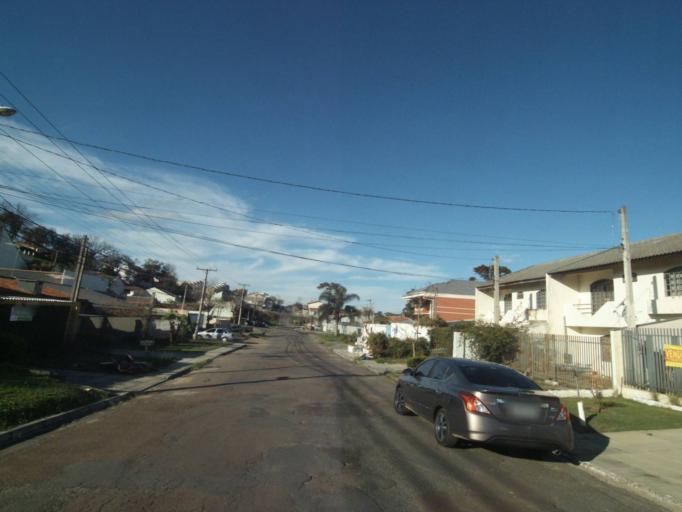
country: BR
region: Parana
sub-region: Curitiba
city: Curitiba
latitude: -25.3861
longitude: -49.2524
